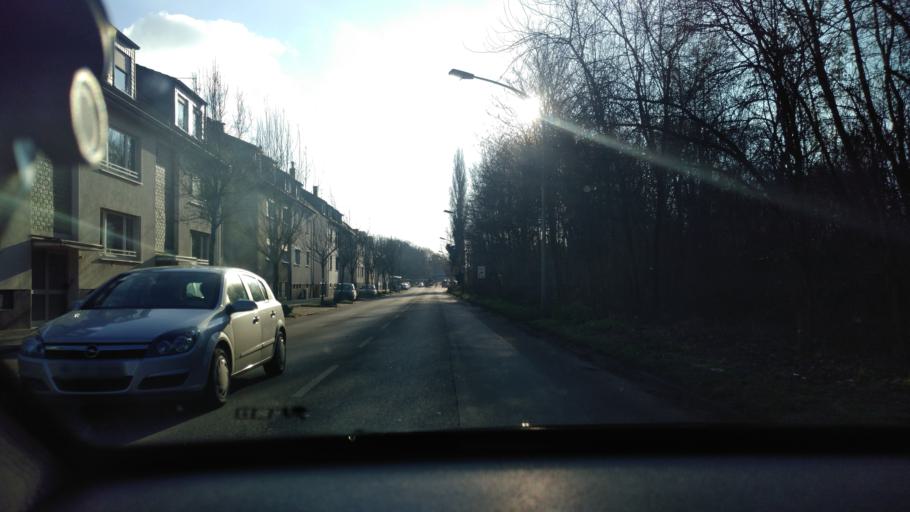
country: DE
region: North Rhine-Westphalia
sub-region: Regierungsbezirk Dusseldorf
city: Essen
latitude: 51.4913
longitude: 6.9804
